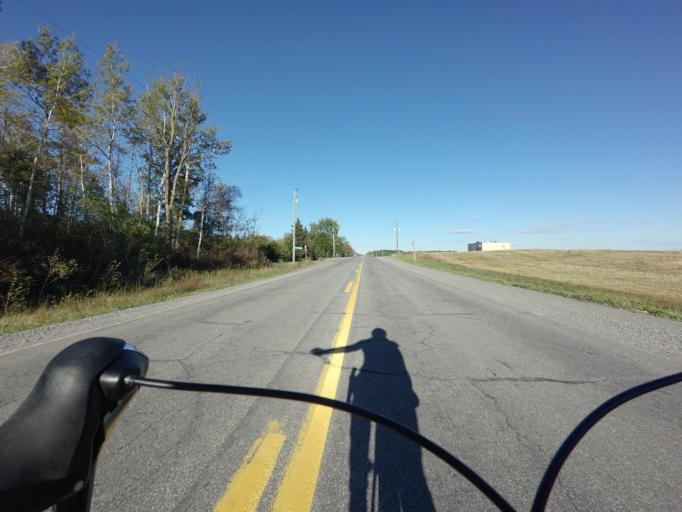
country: CA
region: Ontario
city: Bells Corners
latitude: 45.1900
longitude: -75.7853
